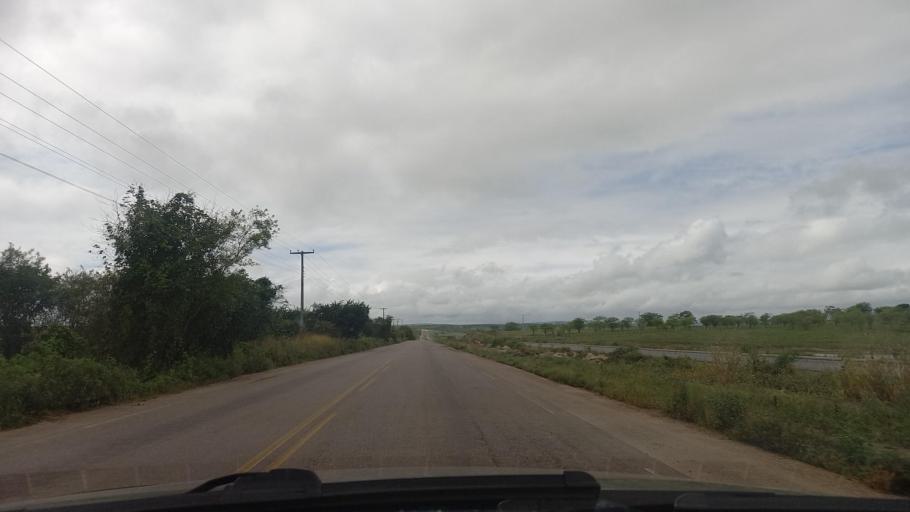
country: BR
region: Alagoas
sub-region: Batalha
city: Batalha
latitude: -9.6459
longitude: -37.1889
